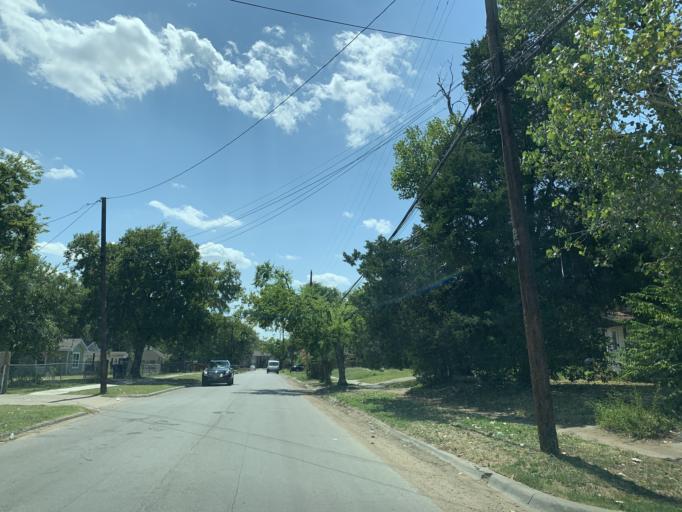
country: US
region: Texas
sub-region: Dallas County
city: Dallas
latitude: 32.7131
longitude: -96.7727
